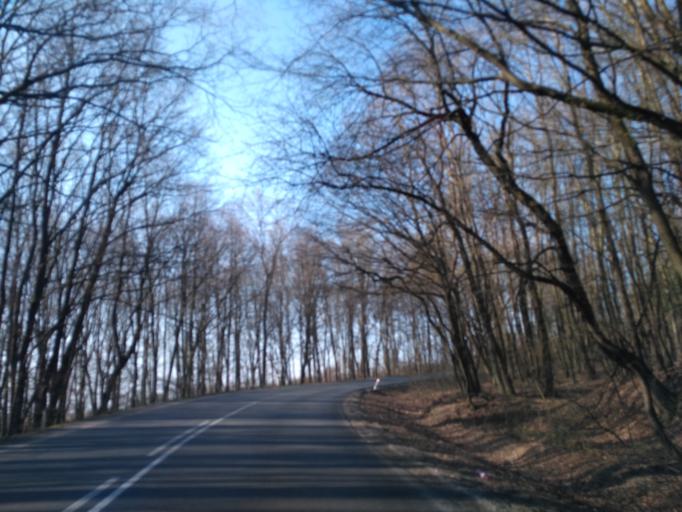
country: SK
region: Kosicky
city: Kosice
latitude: 48.6751
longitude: 21.1583
